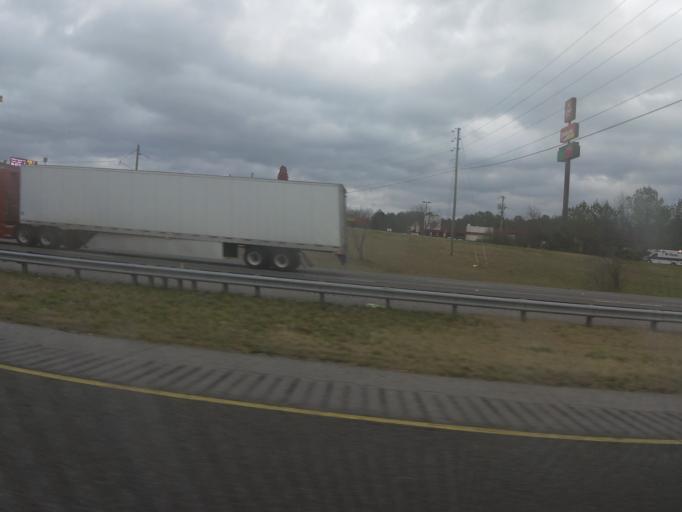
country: US
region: Georgia
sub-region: Whitfield County
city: Dalton
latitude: 34.6872
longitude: -85.0020
